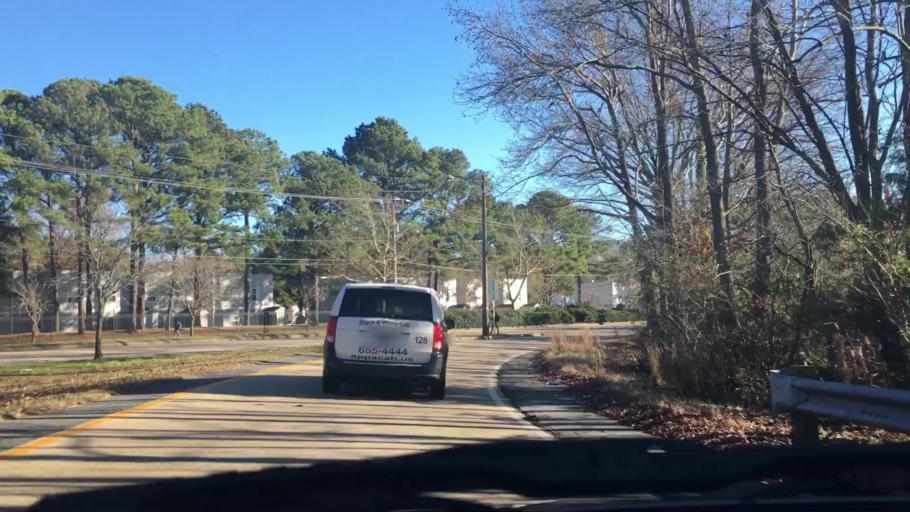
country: US
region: Virginia
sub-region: City of Norfolk
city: Norfolk
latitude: 36.9019
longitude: -76.2400
